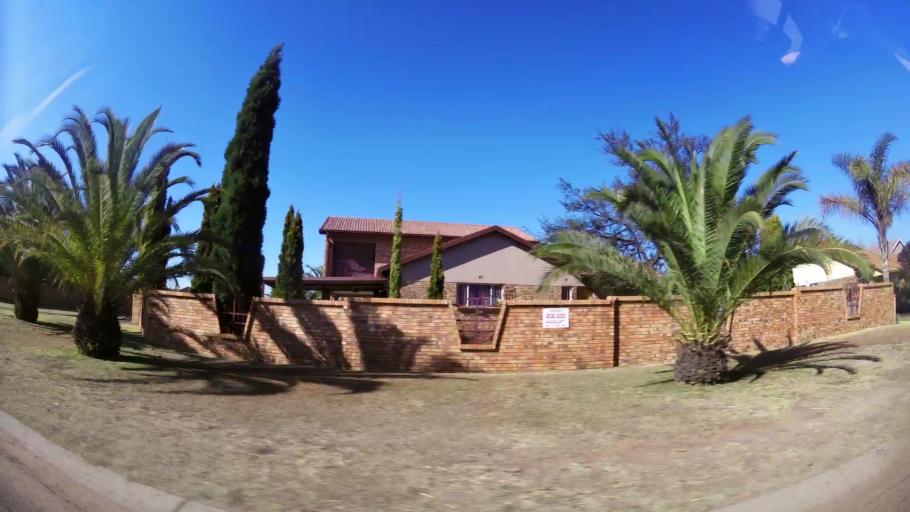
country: ZA
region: Mpumalanga
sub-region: Nkangala District Municipality
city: Witbank
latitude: -25.8857
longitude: 29.2541
